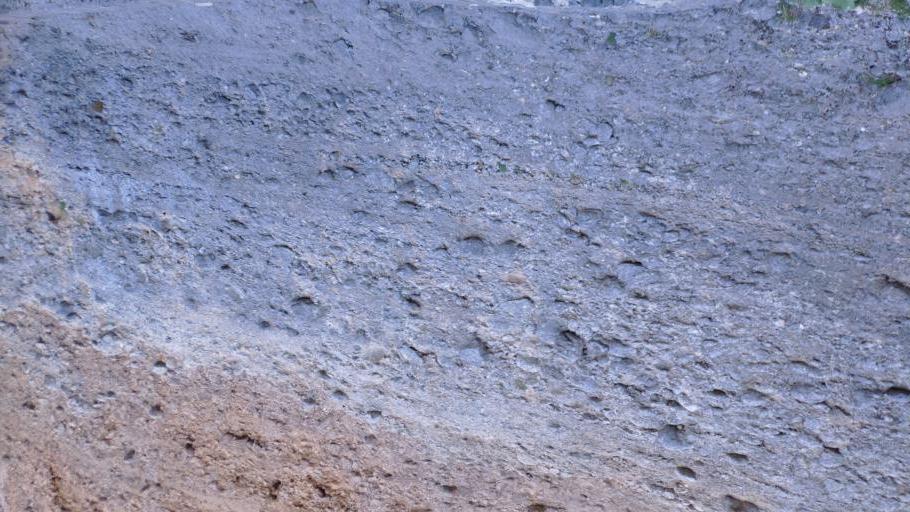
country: GR
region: West Greece
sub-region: Nomos Achaias
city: Aiyira
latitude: 37.9832
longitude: 22.3419
